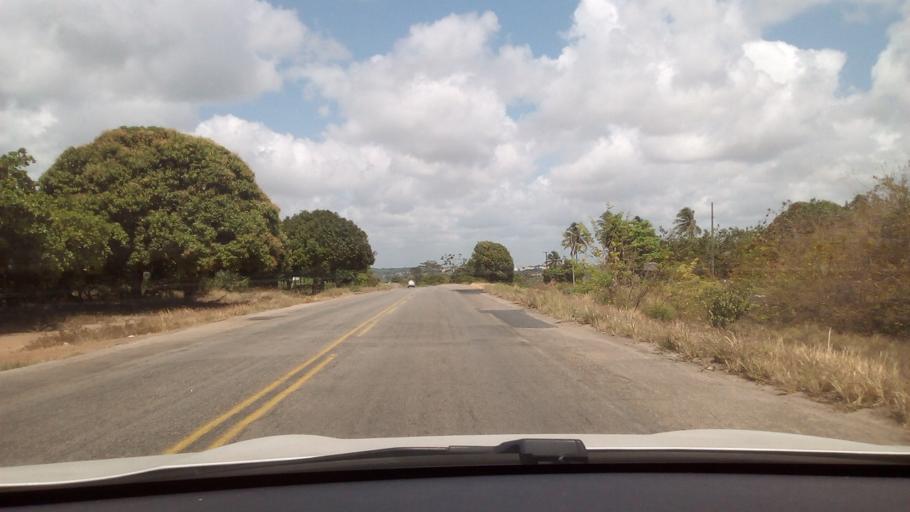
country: BR
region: Paraiba
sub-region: Conde
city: Conde
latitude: -7.2471
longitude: -34.8292
